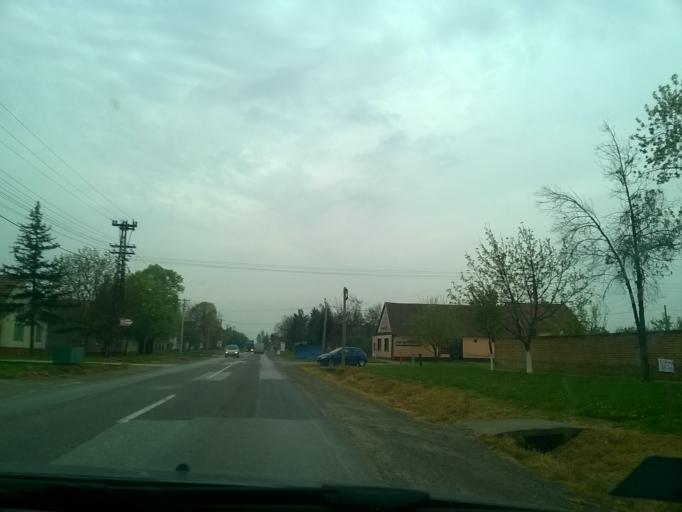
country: RS
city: Hrtkovci
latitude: 44.8730
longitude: 19.7697
